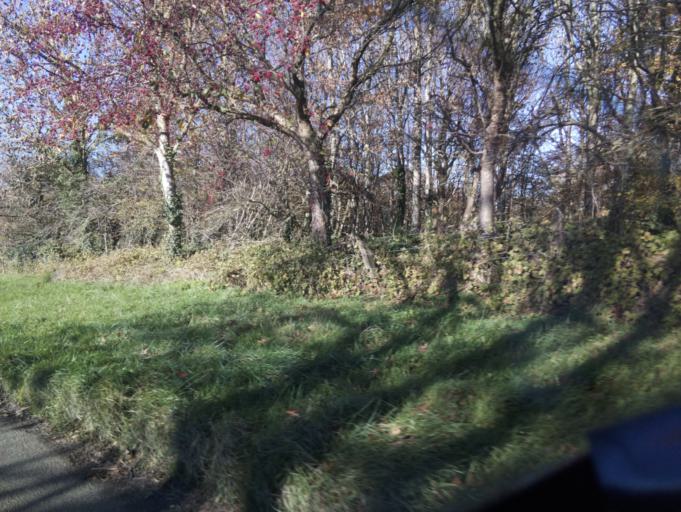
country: GB
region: England
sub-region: Somerset
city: Yeovil
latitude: 50.8969
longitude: -2.6113
